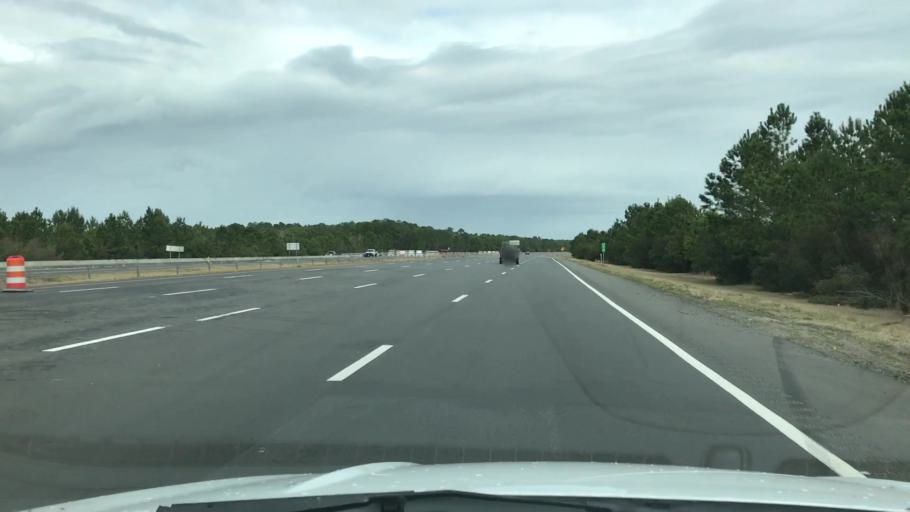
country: US
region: South Carolina
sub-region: Horry County
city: Socastee
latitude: 33.7051
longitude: -79.0121
